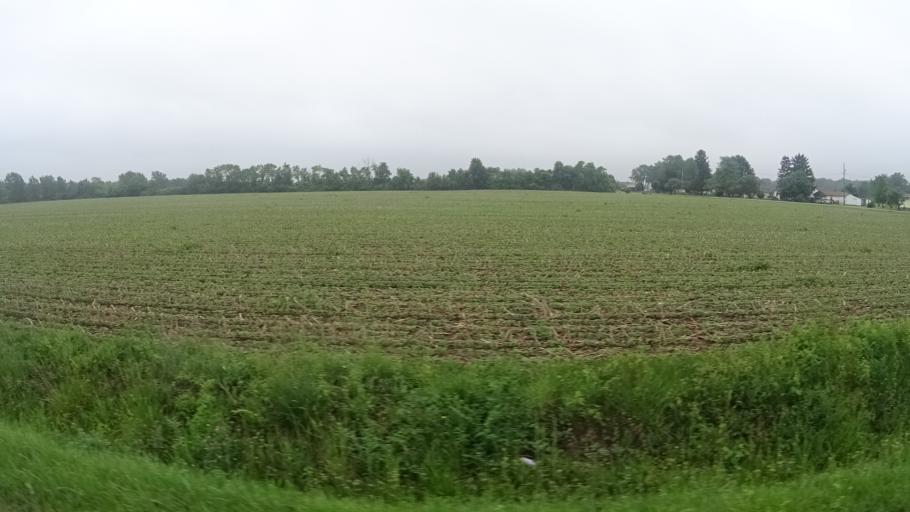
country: US
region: Ohio
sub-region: Erie County
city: Sandusky
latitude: 41.3614
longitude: -82.7723
